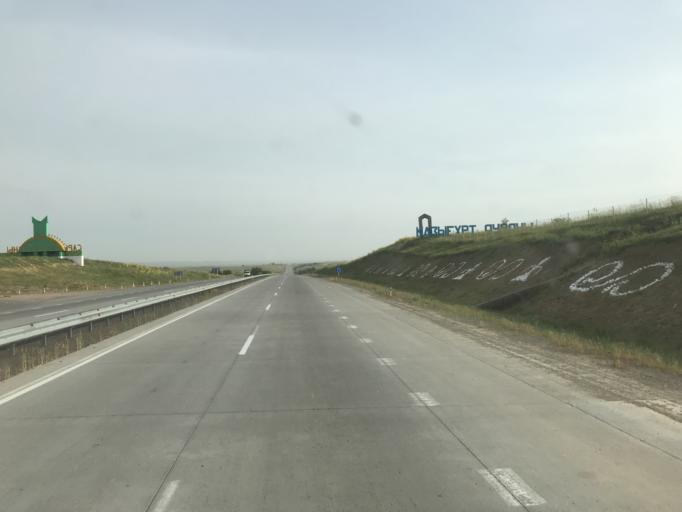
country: KZ
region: Ongtustik Qazaqstan
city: Qazyqurt
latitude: 41.6062
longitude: 69.4043
